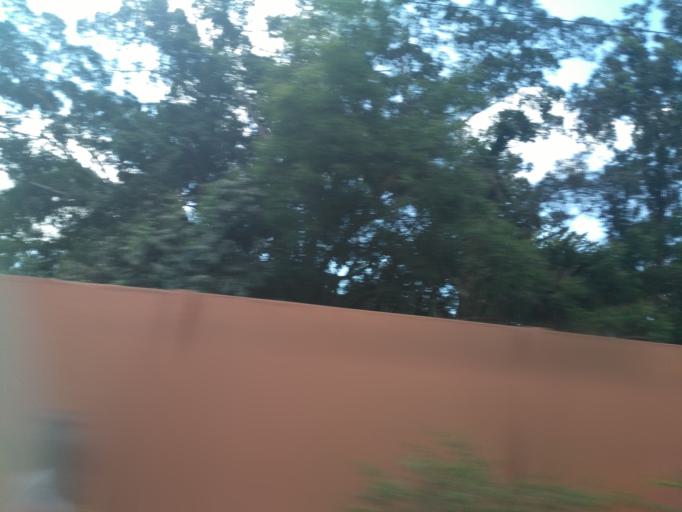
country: TZ
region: Mwanza
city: Mwanza
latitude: -2.5139
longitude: 32.9078
